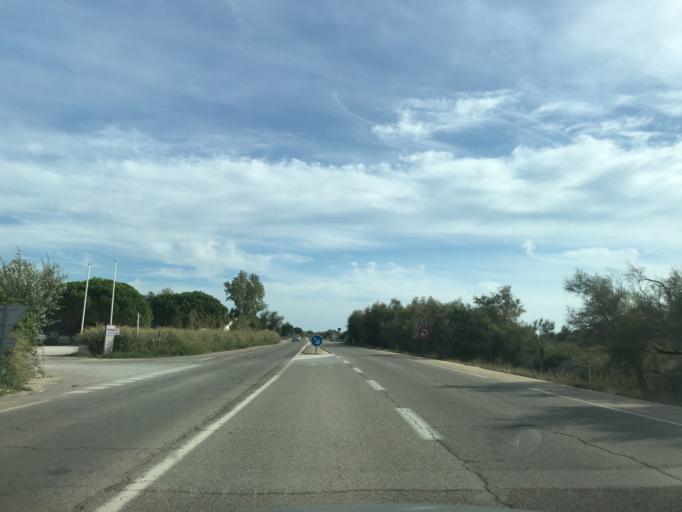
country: FR
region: Provence-Alpes-Cote d'Azur
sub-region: Departement des Bouches-du-Rhone
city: Saintes-Maries-de-la-Mer
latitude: 43.4905
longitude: 4.4035
